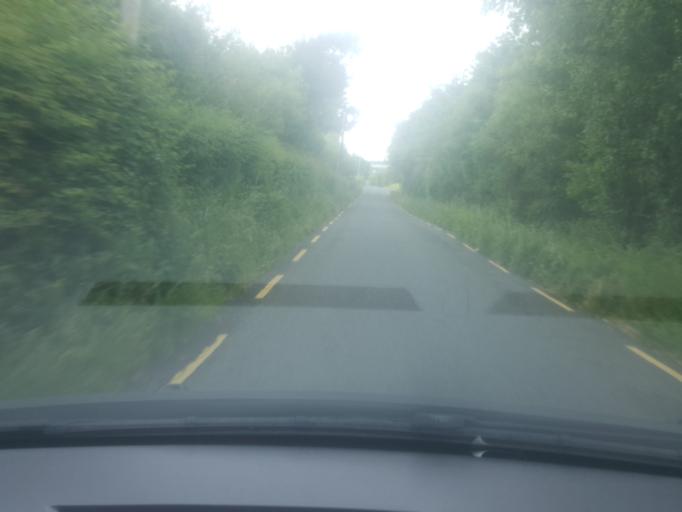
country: IE
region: Munster
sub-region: Ciarrai
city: Cill Airne
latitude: 52.1006
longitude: -9.5061
